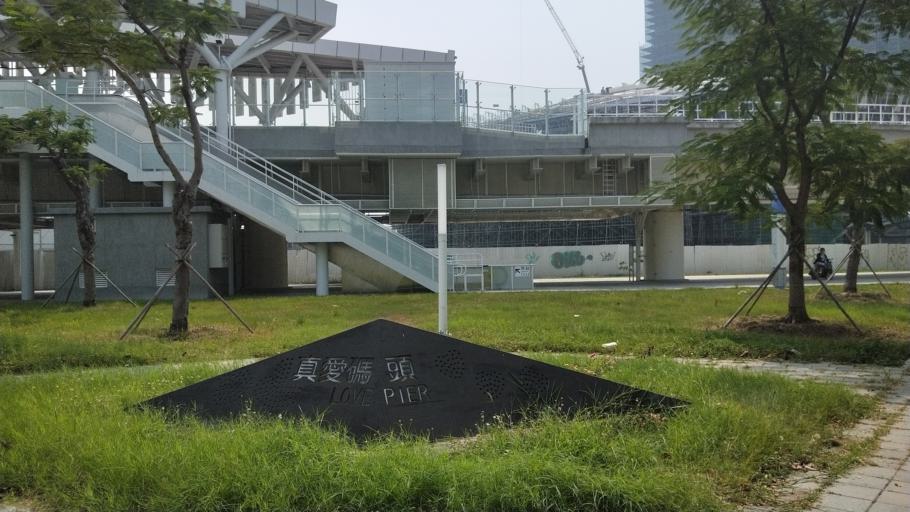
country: TW
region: Kaohsiung
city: Kaohsiung
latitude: 22.6196
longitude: 120.2892
